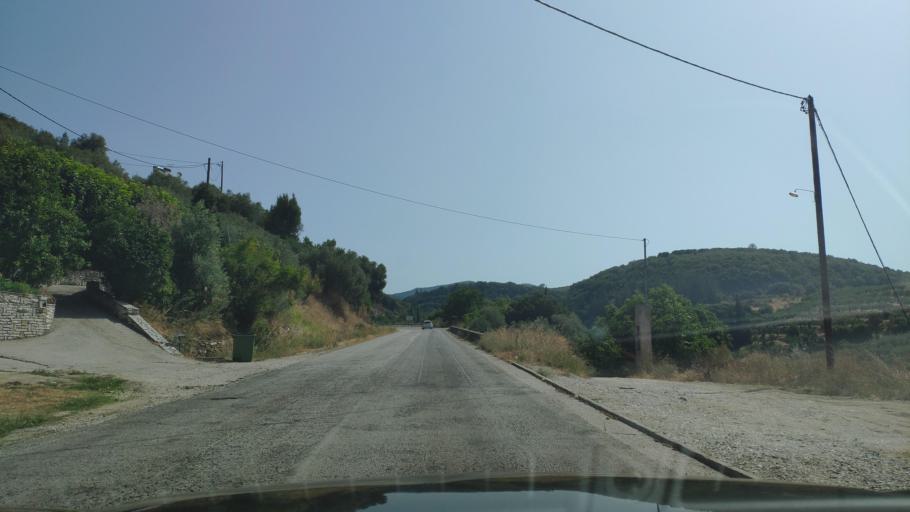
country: GR
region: Epirus
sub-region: Nomos Artas
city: Peta
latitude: 39.1582
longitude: 21.0302
